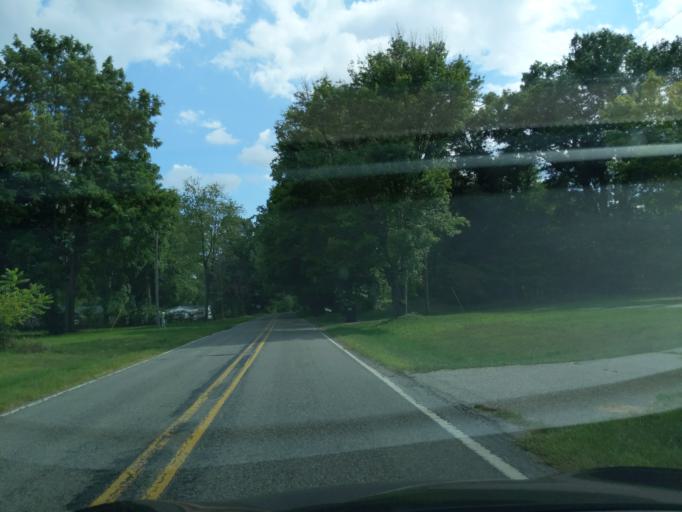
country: US
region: Michigan
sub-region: Jackson County
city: Spring Arbor
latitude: 42.3427
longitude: -84.5509
